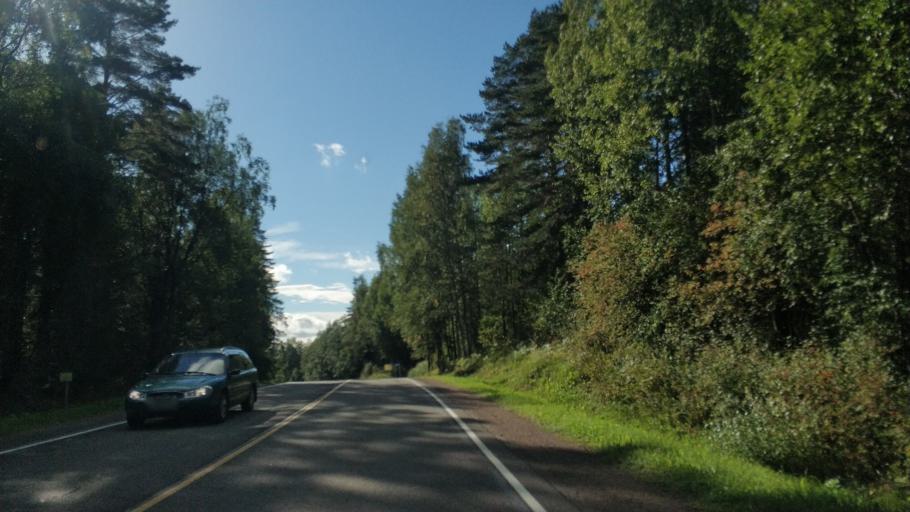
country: RU
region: Republic of Karelia
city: Khelyulya
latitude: 61.6553
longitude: 30.6189
